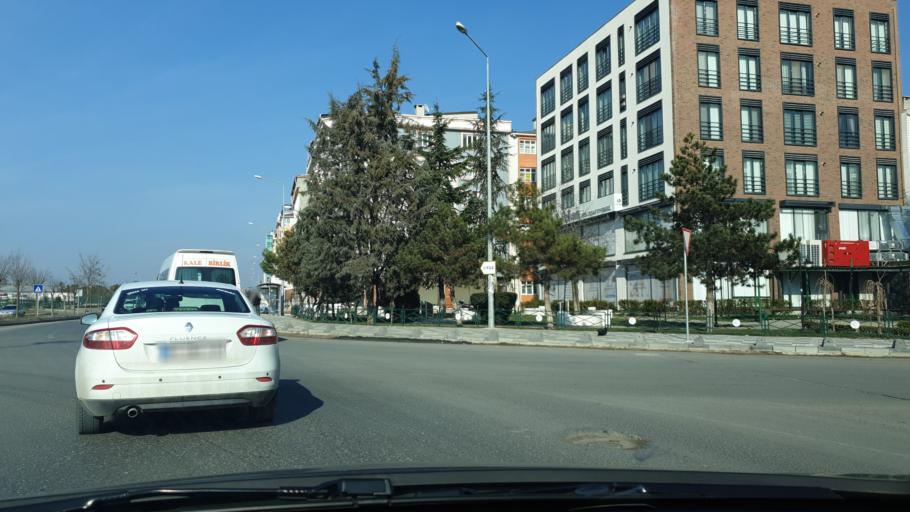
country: TR
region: Tekirdag
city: Cerkezkoey
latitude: 41.2913
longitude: 27.9935
